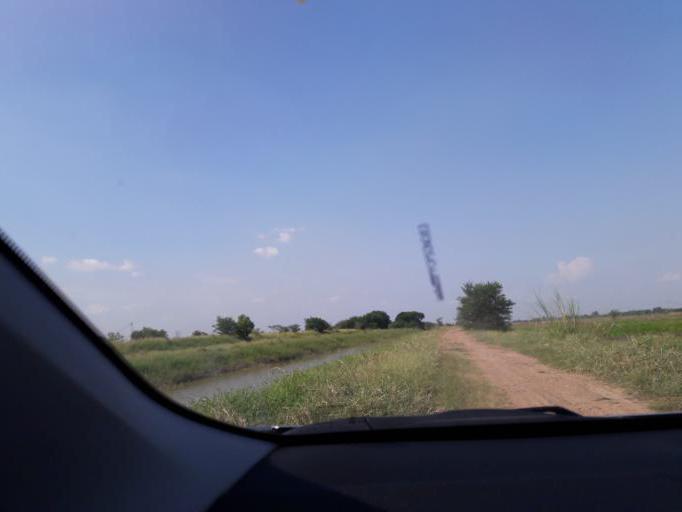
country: TH
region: Ang Thong
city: Ang Thong
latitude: 14.5522
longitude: 100.4066
